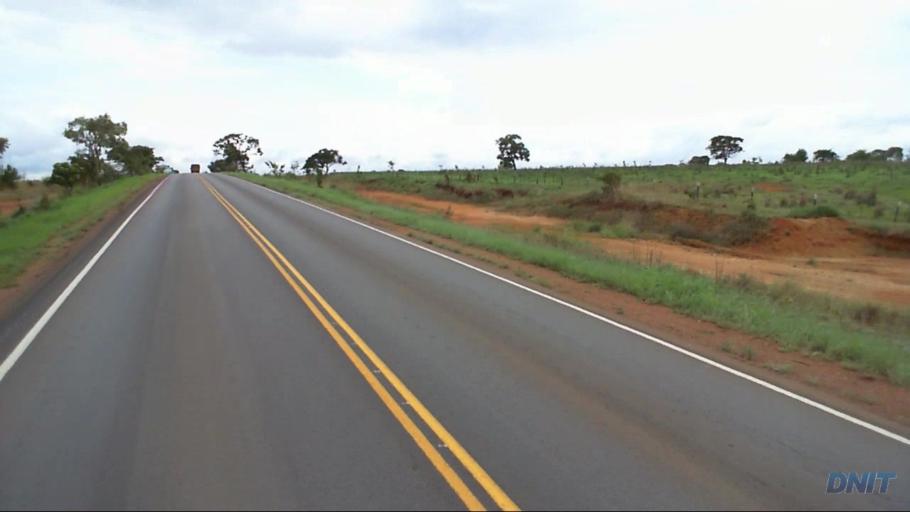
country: BR
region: Goias
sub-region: Padre Bernardo
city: Padre Bernardo
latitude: -15.2933
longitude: -48.2421
